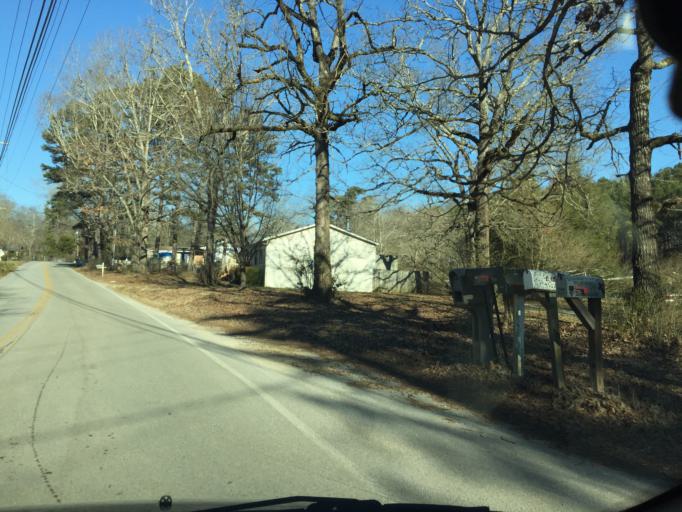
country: US
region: Tennessee
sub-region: Hamilton County
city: Collegedale
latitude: 35.0580
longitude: -85.0927
